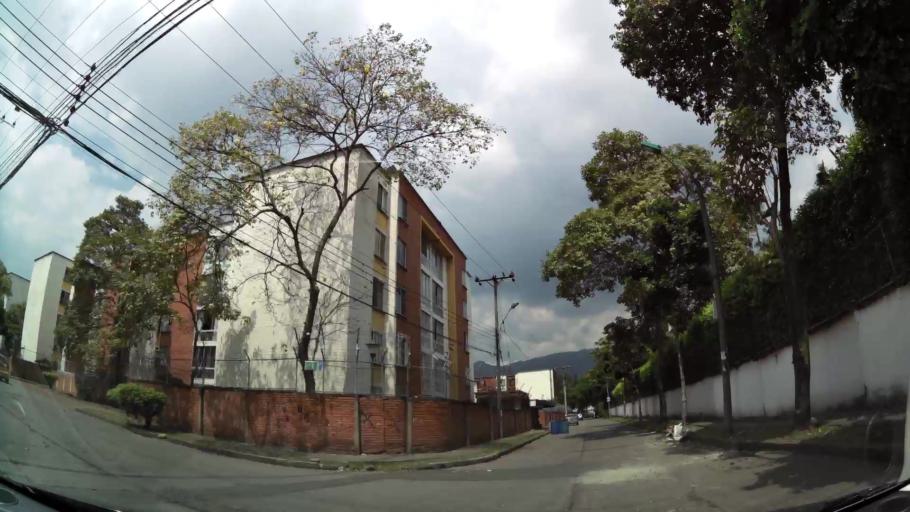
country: CO
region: Valle del Cauca
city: Cali
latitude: 3.4854
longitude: -76.5103
